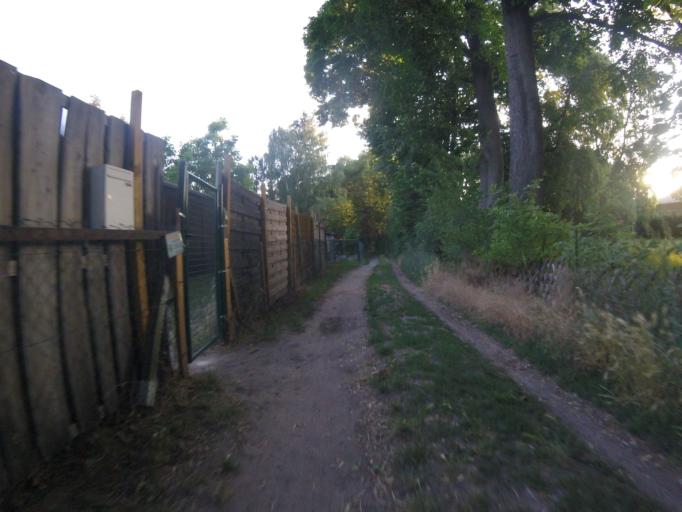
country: DE
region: Brandenburg
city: Mittenwalde
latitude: 52.2625
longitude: 13.5404
